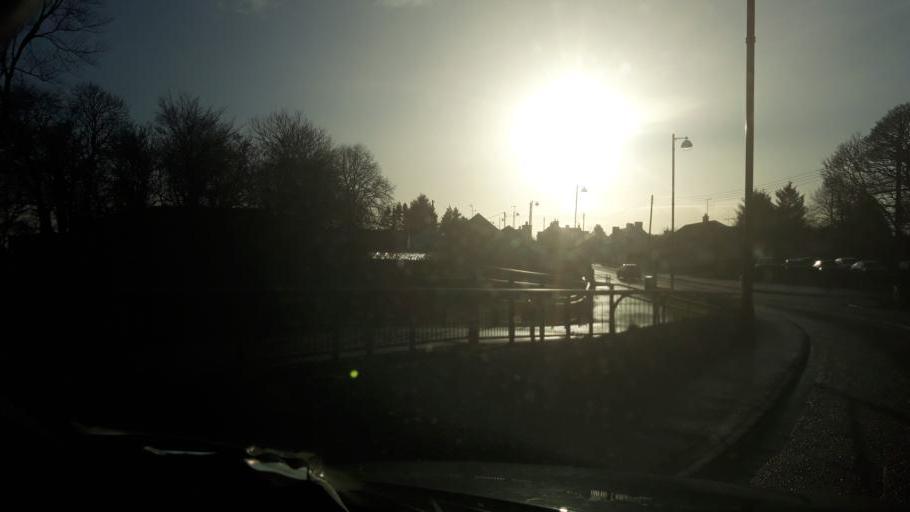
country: GB
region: Northern Ireland
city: Maghera
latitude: 54.9079
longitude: -6.6671
